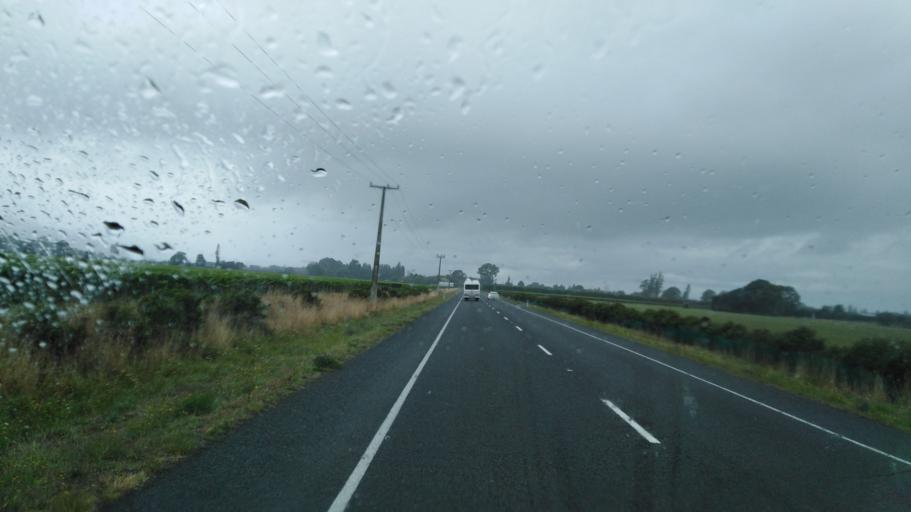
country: NZ
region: Marlborough
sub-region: Marlborough District
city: Blenheim
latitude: -41.4616
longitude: 173.9378
